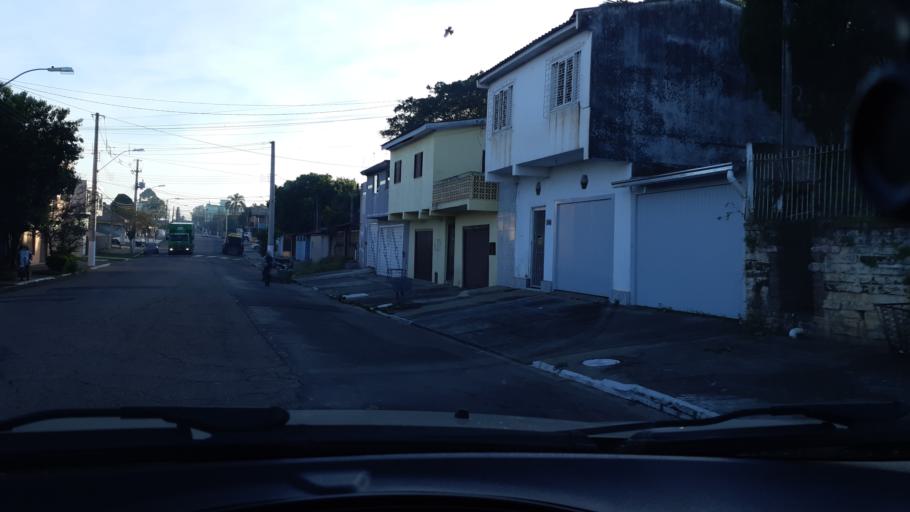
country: BR
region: Rio Grande do Sul
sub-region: Sapucaia Do Sul
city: Sapucaia
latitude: -29.8489
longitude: -51.1527
